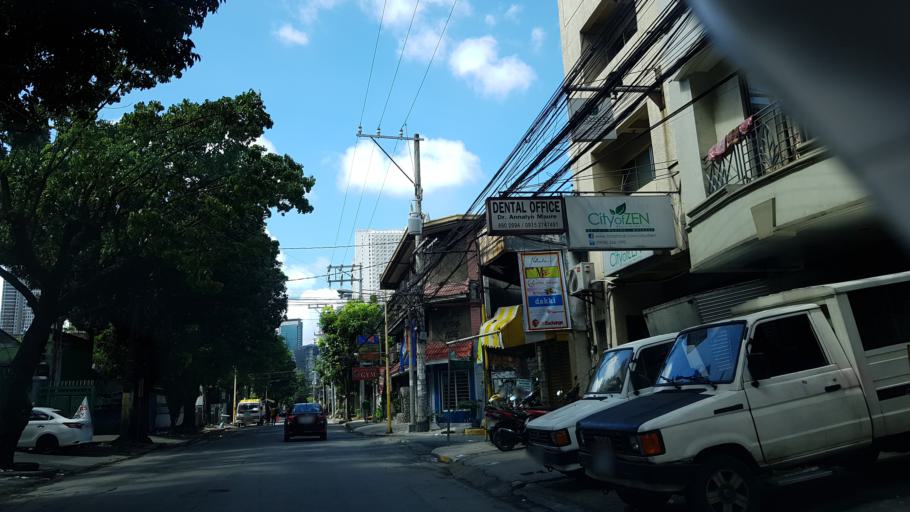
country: PH
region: Metro Manila
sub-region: Makati City
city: Makati City
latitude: 14.5690
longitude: 121.0244
